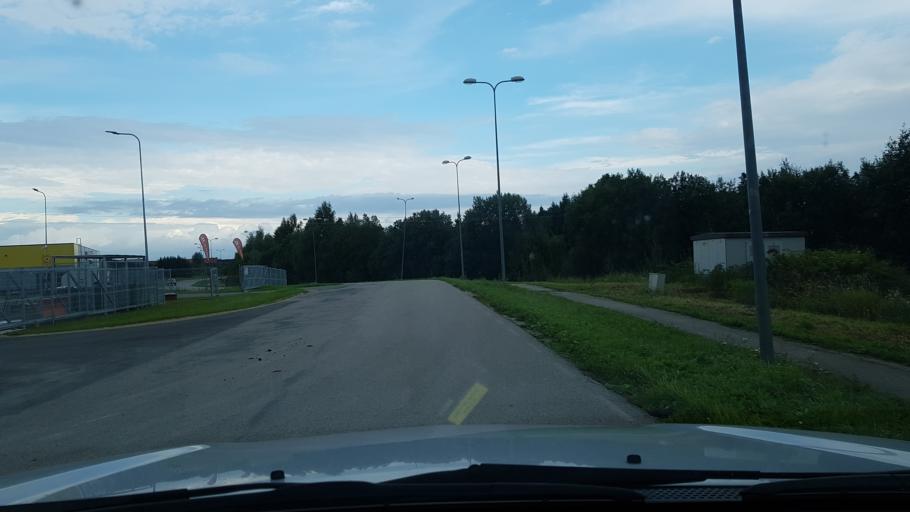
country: EE
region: Harju
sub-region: Rae vald
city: Jueri
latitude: 59.3444
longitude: 24.8993
